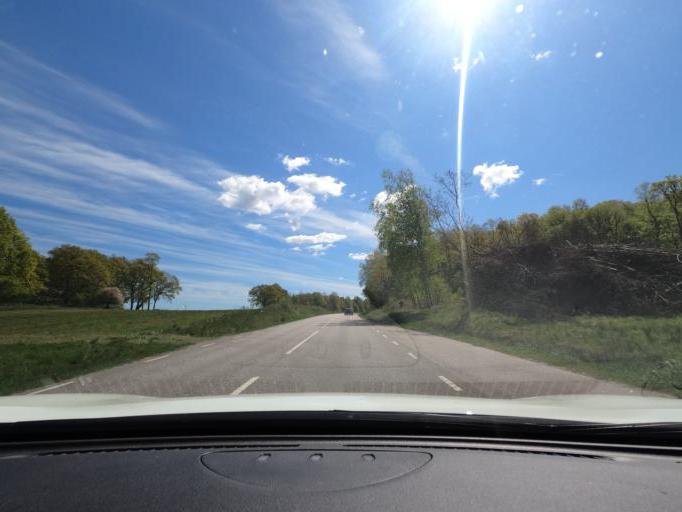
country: SE
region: Halland
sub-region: Kungsbacka Kommun
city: Fjaeras kyrkby
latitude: 57.4358
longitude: 12.1783
